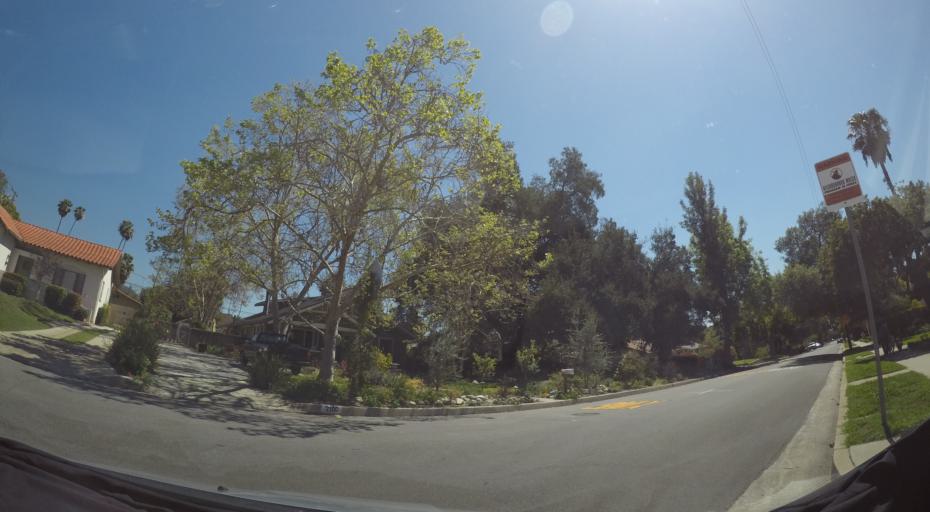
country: US
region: California
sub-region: Los Angeles County
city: Altadena
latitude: 34.1821
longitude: -118.1286
